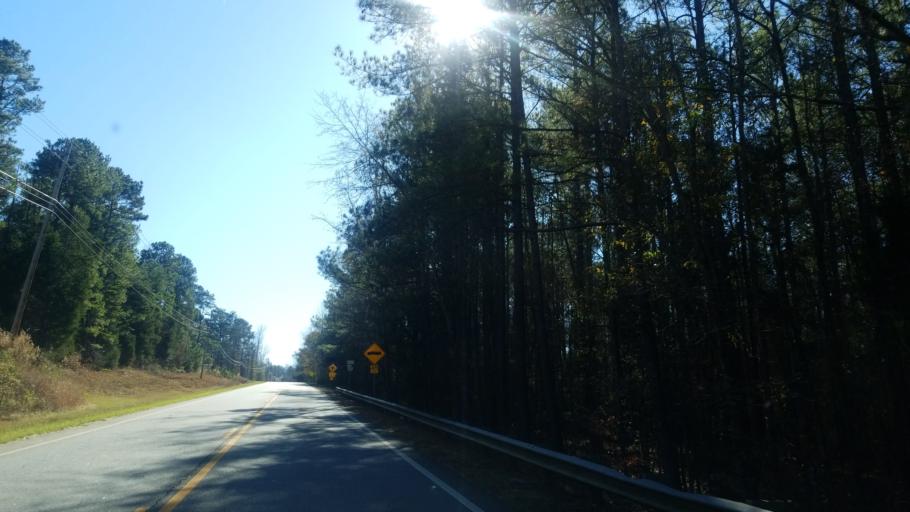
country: US
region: Alabama
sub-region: Lee County
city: Smiths Station
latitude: 32.5845
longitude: -85.0206
